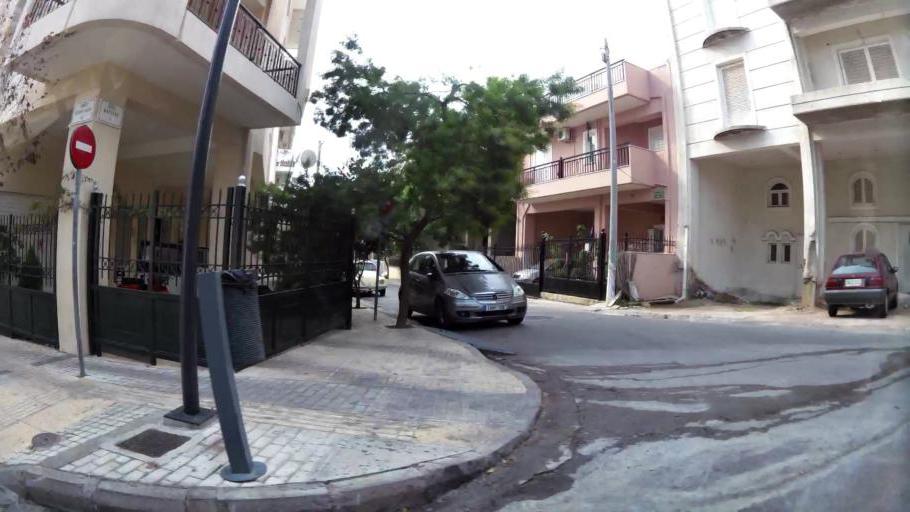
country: GR
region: Attica
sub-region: Nomarchia Athinas
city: Petroupolis
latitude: 38.0289
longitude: 23.6761
